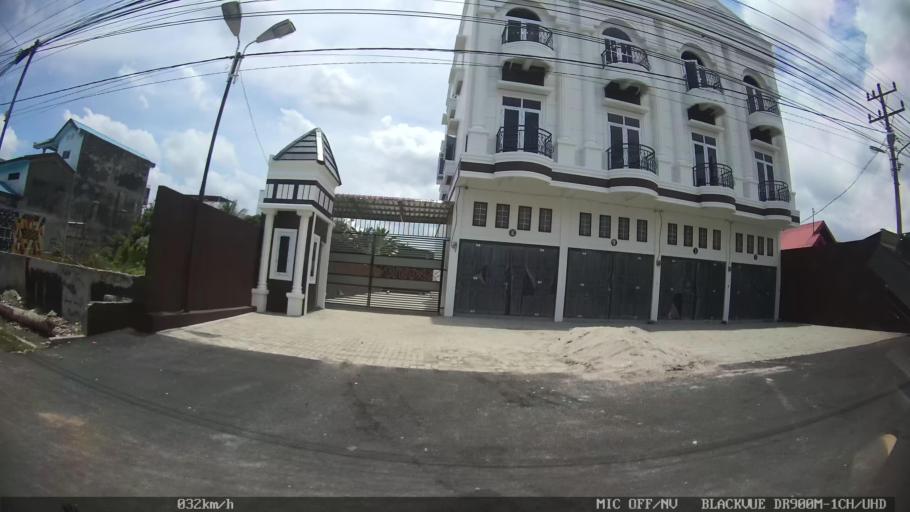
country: ID
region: North Sumatra
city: Medan
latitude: 3.6161
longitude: 98.6960
